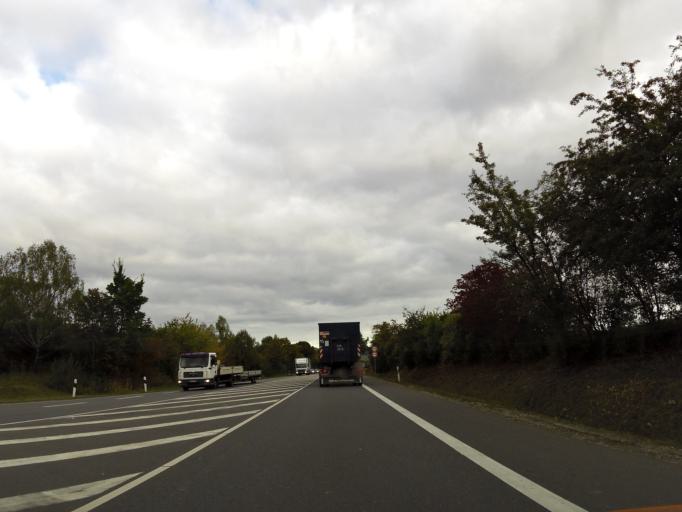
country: DE
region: Lower Saxony
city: Northeim
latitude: 51.7351
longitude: 9.9728
